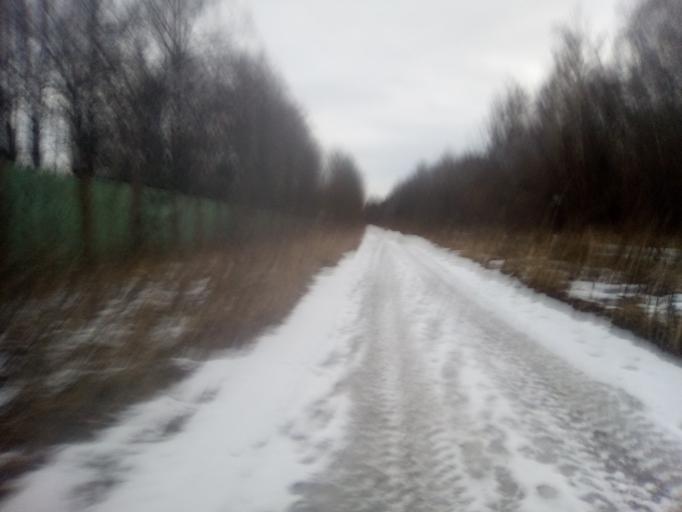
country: RU
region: Moskovskaya
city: Filimonki
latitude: 55.5126
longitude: 37.3962
